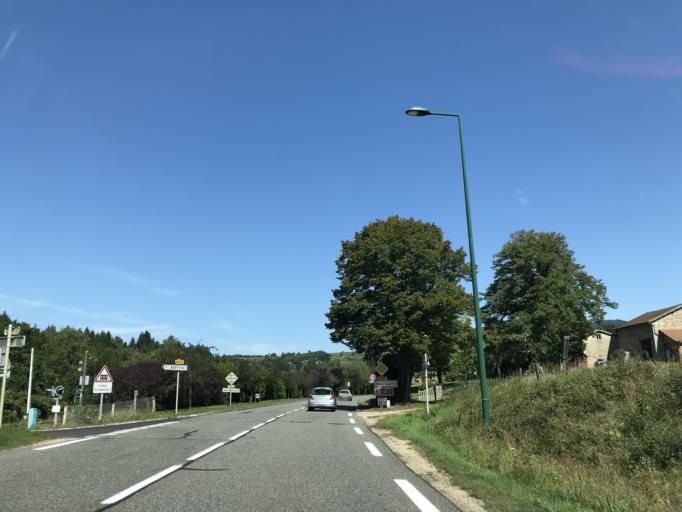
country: FR
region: Auvergne
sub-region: Departement du Puy-de-Dome
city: Job
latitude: 45.6390
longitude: 3.7064
